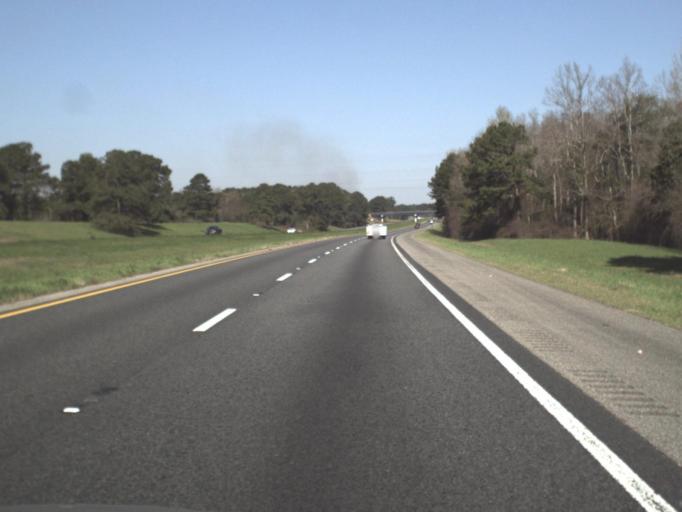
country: US
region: Florida
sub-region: Gadsden County
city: Gretna
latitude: 30.5905
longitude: -84.7195
